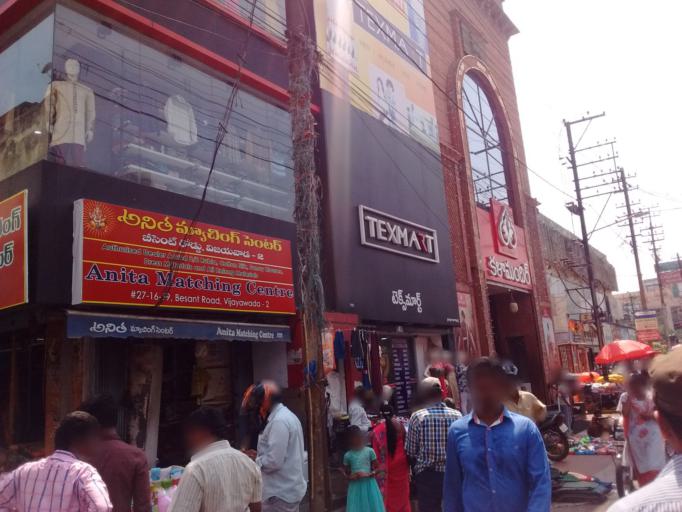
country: IN
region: Andhra Pradesh
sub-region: Krishna
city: Vijayawada
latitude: 16.5112
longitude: 80.6267
